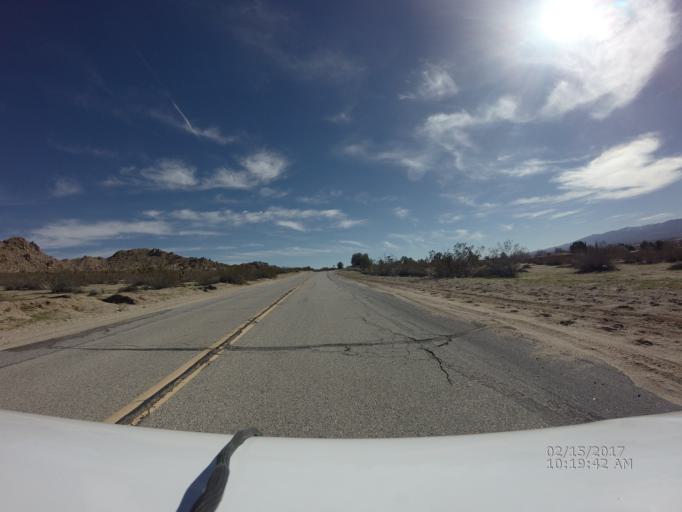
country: US
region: California
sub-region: Los Angeles County
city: Lake Los Angeles
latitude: 34.5874
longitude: -117.8614
